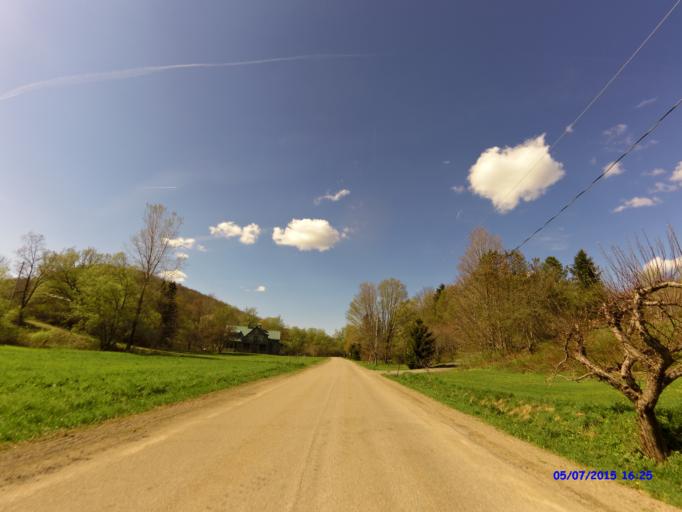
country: US
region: New York
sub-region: Cattaraugus County
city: Little Valley
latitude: 42.2903
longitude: -78.6781
